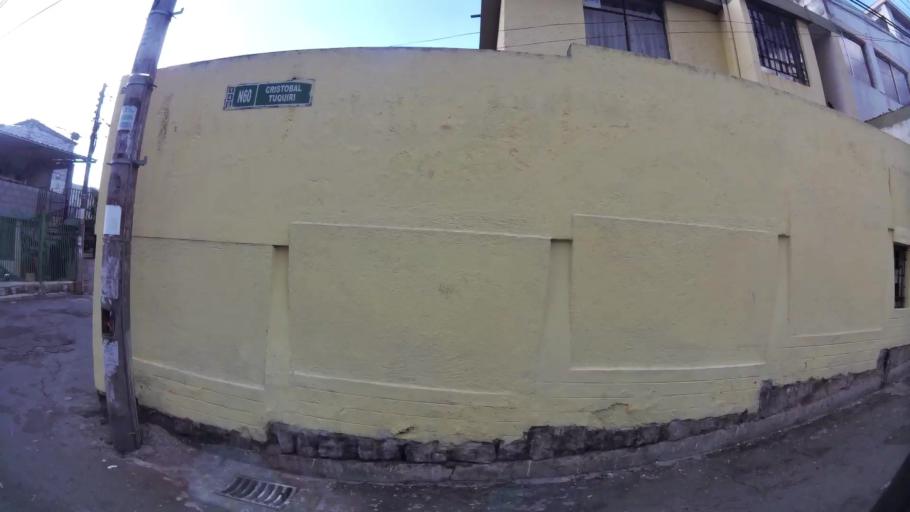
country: EC
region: Pichincha
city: Quito
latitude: -0.1259
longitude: -78.4881
